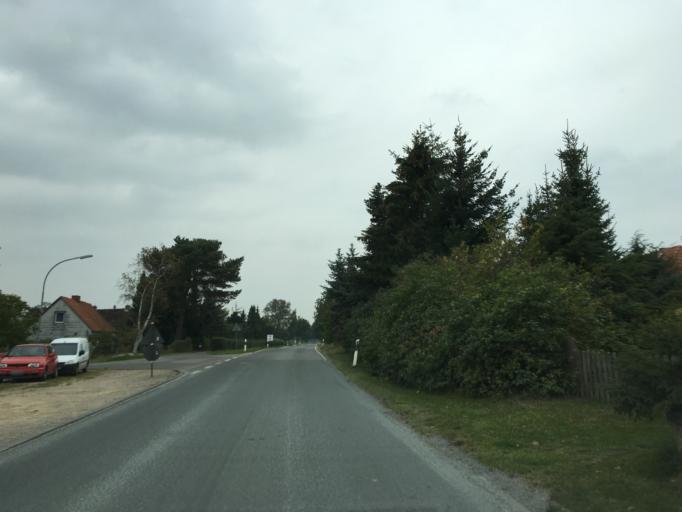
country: DE
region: Schleswig-Holstein
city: Seedorf
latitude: 53.6225
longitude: 10.8599
